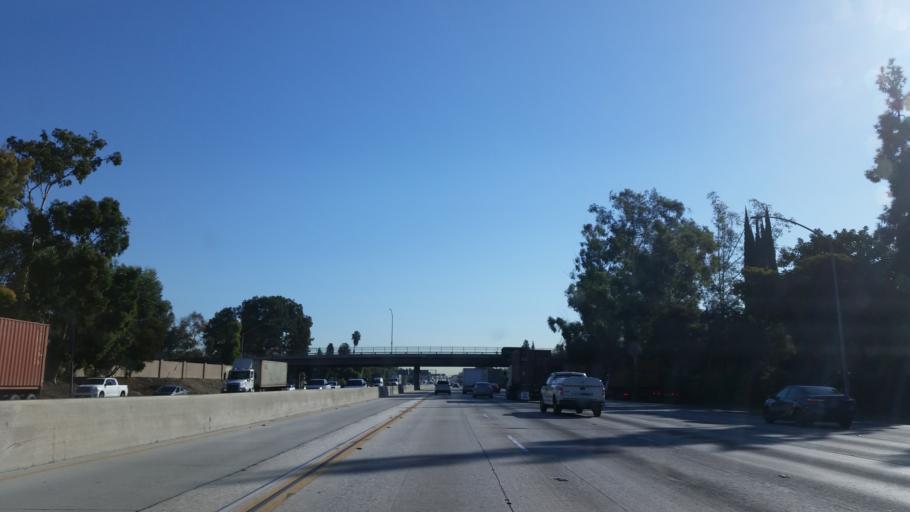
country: US
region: California
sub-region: Los Angeles County
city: Artesia
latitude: 33.8764
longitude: -118.0934
